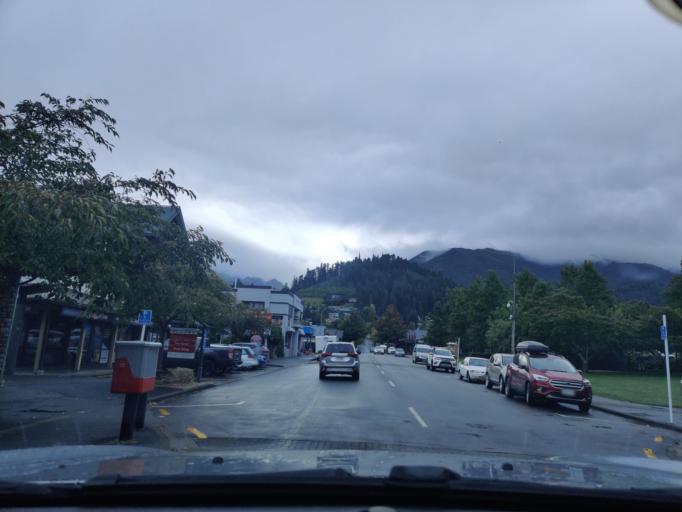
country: NZ
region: Canterbury
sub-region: Hurunui District
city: Amberley
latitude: -42.5214
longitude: 172.8296
